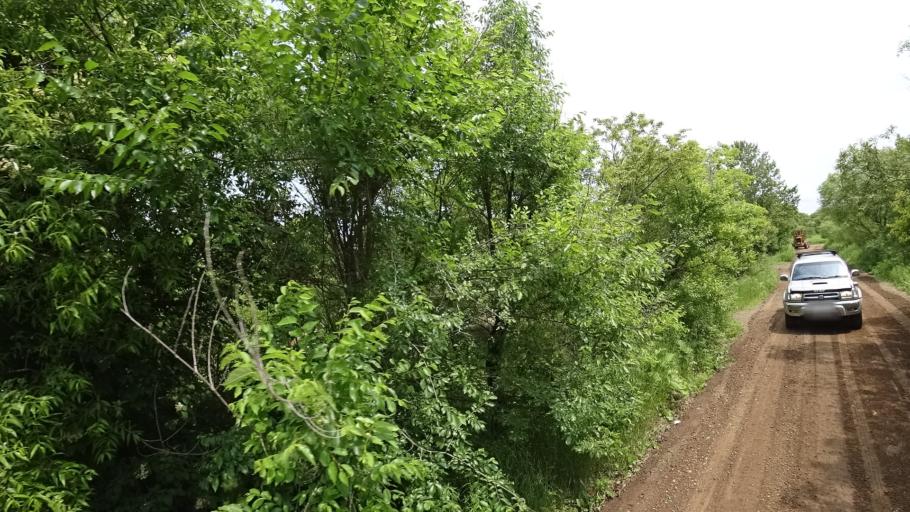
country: RU
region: Primorskiy
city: Novosysoyevka
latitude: 44.2413
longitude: 133.3759
